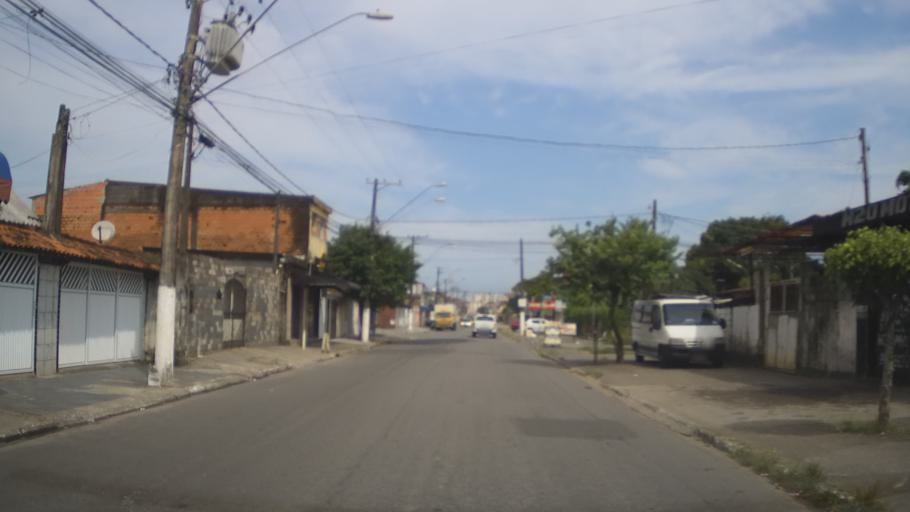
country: BR
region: Sao Paulo
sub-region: Praia Grande
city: Praia Grande
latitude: -24.0010
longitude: -46.4459
